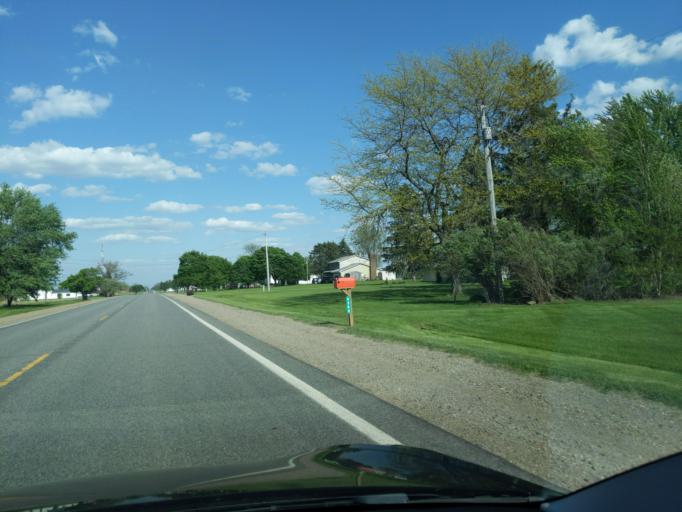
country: US
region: Michigan
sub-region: Ionia County
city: Portland
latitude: 42.7556
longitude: -84.9246
